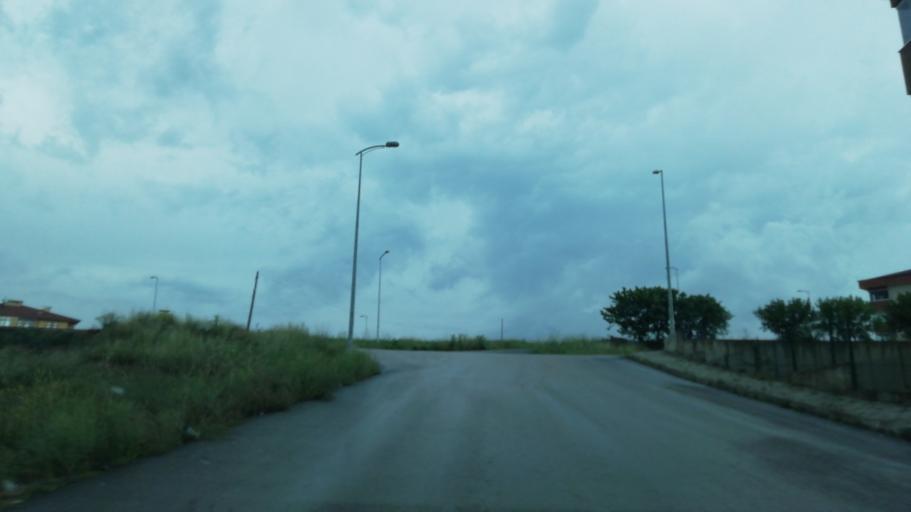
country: TR
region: Karabuk
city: Safranbolu
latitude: 41.2383
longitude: 32.6816
